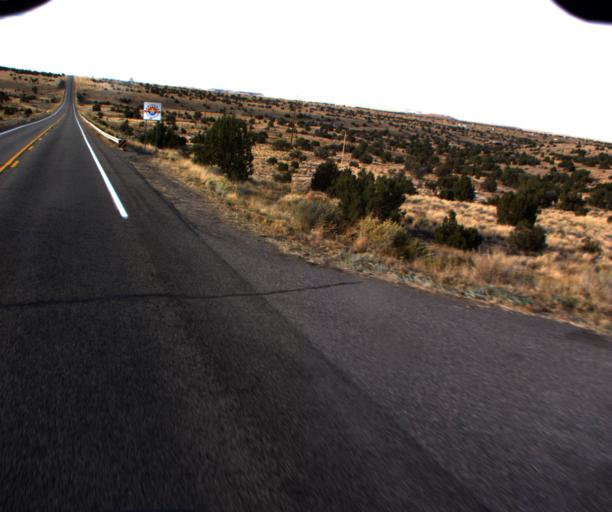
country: US
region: New Mexico
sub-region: San Juan County
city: Shiprock
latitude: 36.8811
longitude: -109.0500
